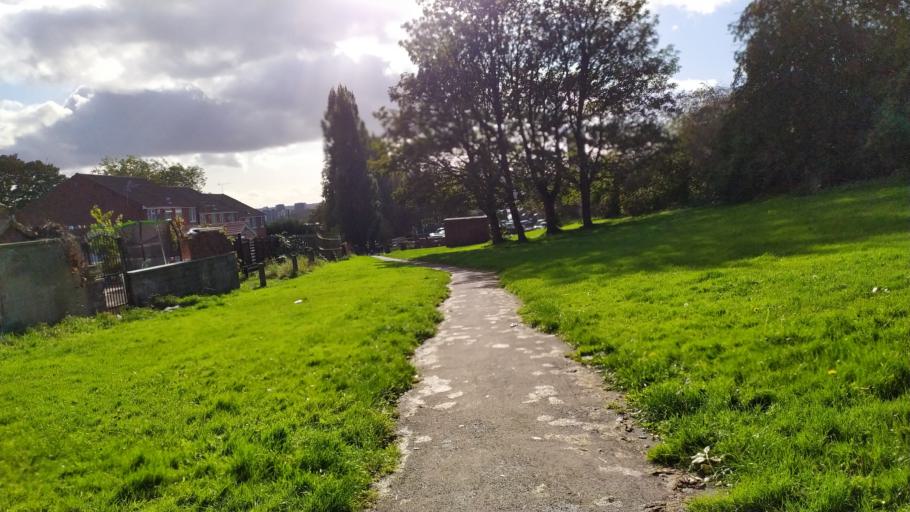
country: GB
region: England
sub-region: City and Borough of Leeds
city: Chapel Allerton
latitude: 53.8147
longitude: -1.5371
